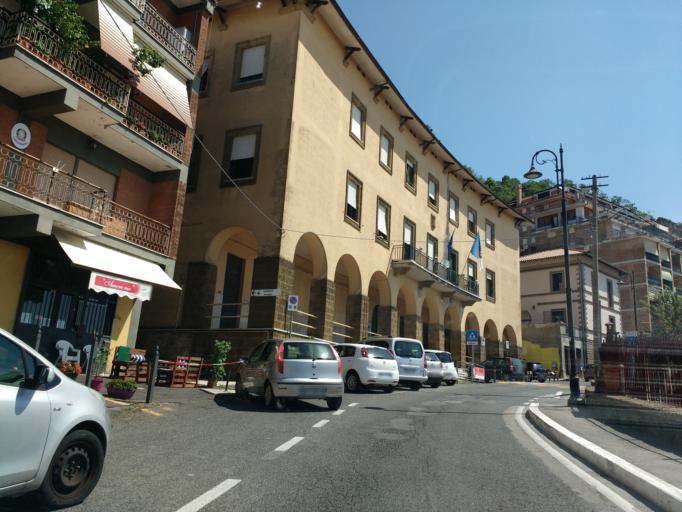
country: IT
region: Latium
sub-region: Citta metropolitana di Roma Capitale
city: Rocca di Papa
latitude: 41.7599
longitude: 12.7081
